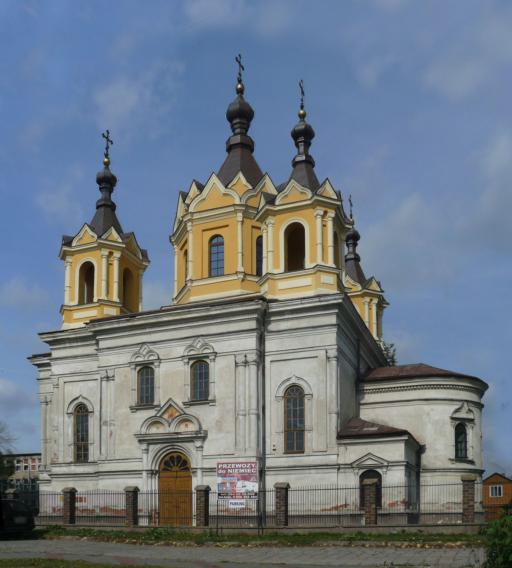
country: PL
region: Lublin Voivodeship
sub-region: Powiat tomaszowski
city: Tomaszow Lubelski
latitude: 50.4530
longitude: 23.4207
